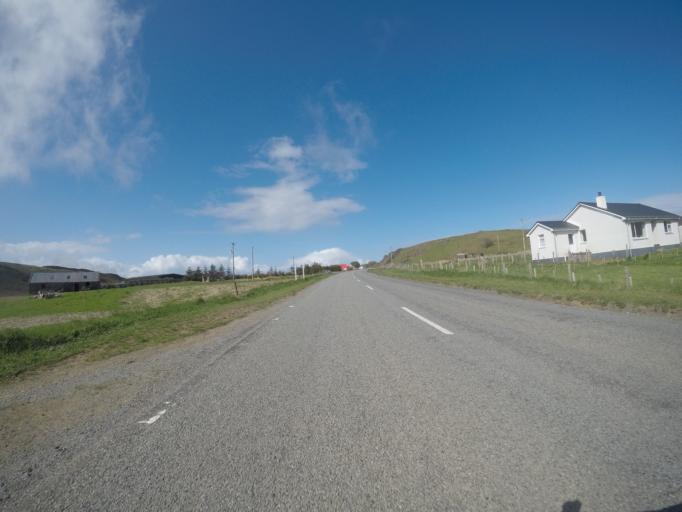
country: GB
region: Scotland
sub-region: Highland
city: Portree
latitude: 57.5839
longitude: -6.1578
